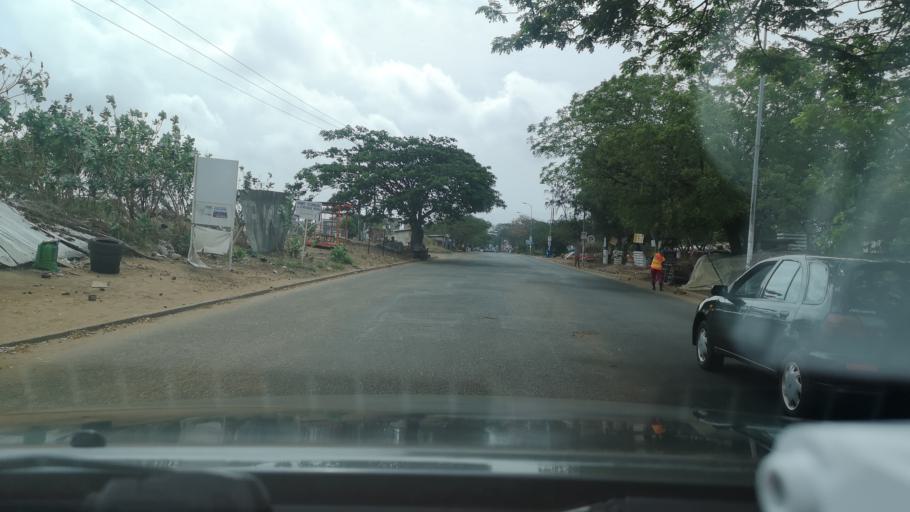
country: GH
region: Greater Accra
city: Nungua
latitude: 5.6234
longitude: -0.0669
